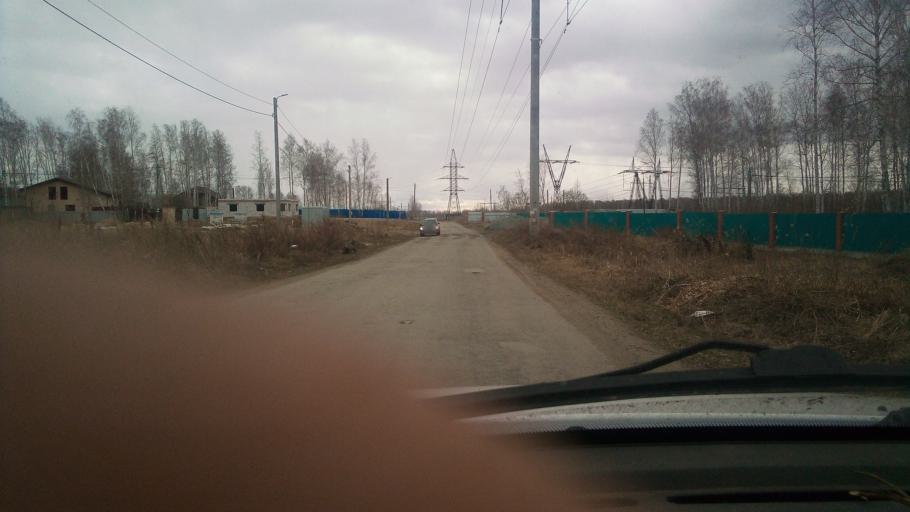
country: RU
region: Chelyabinsk
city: Sargazy
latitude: 55.1298
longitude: 61.2418
